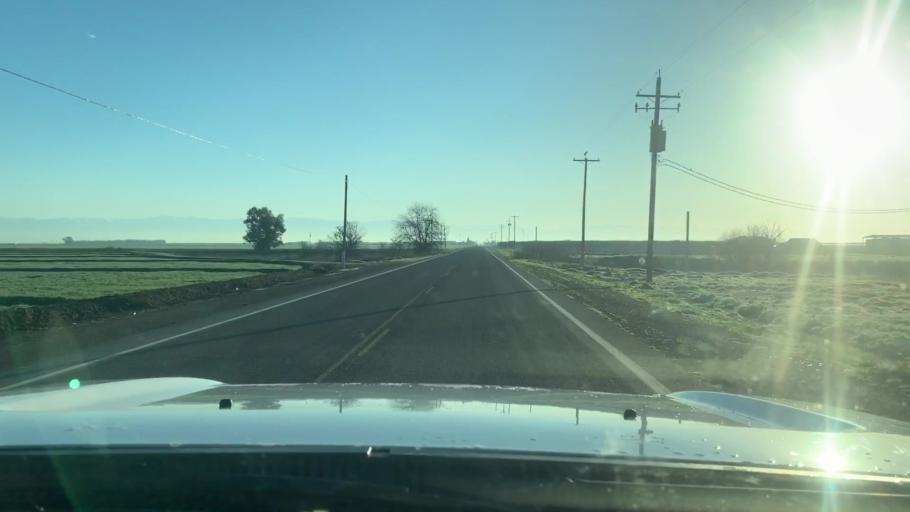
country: US
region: California
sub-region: Kings County
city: Corcoran
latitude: 36.2110
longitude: -119.5643
